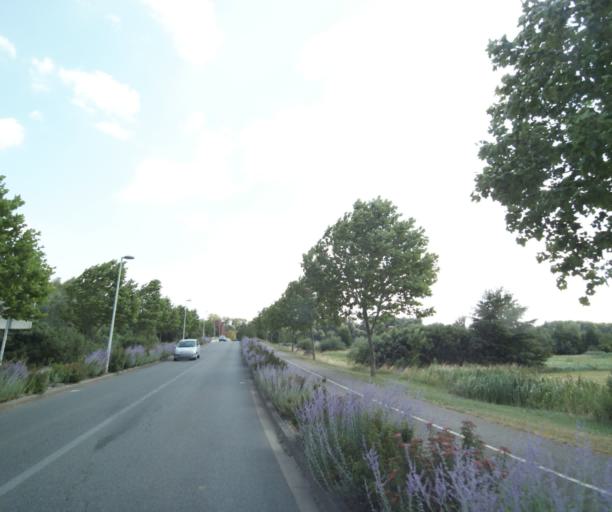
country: FR
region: Lorraine
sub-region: Departement de Meurthe-et-Moselle
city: Luneville
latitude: 48.5995
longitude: 6.4982
